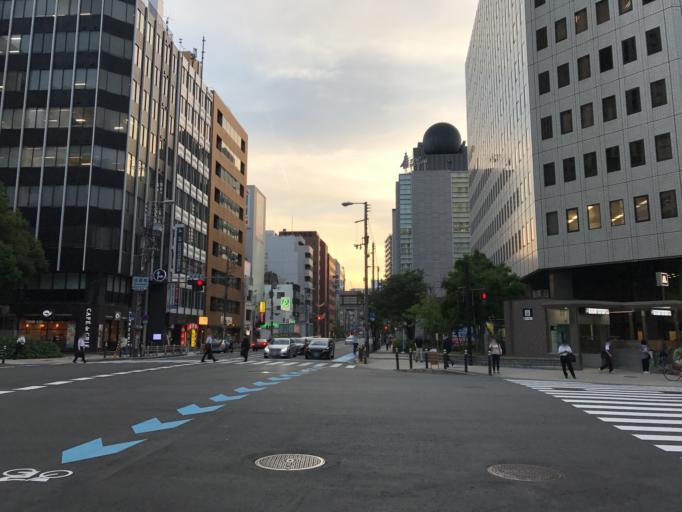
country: JP
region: Osaka
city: Osaka-shi
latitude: 34.6838
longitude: 135.4971
